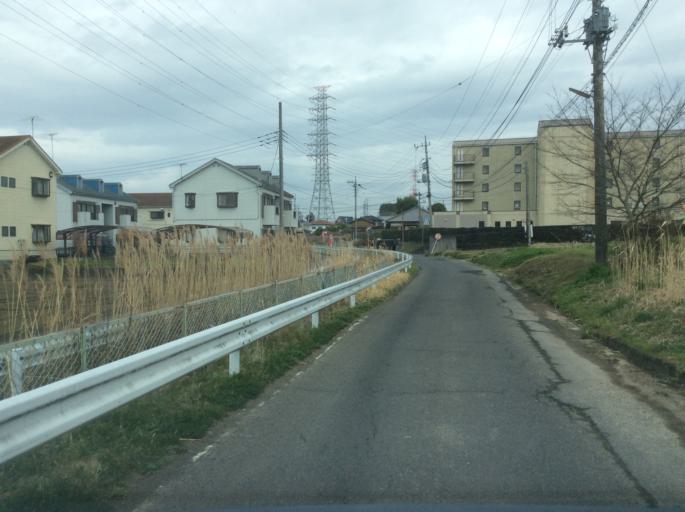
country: JP
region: Ibaraki
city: Ishige
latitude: 36.1737
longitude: 139.9577
